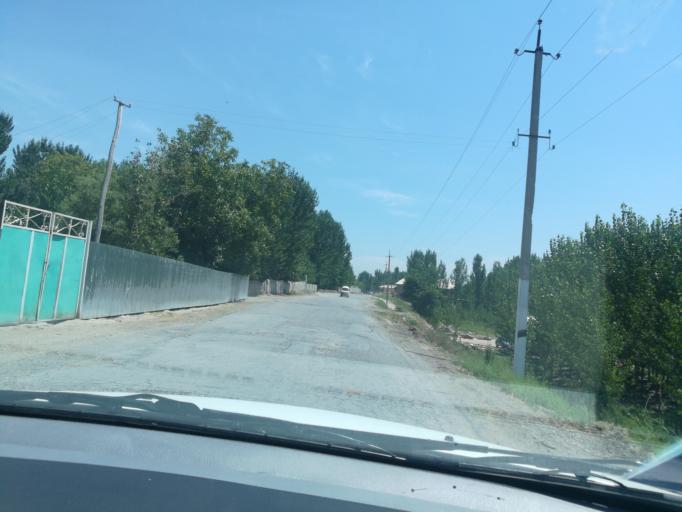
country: UZ
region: Namangan
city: Haqqulobod
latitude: 40.8982
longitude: 72.0061
